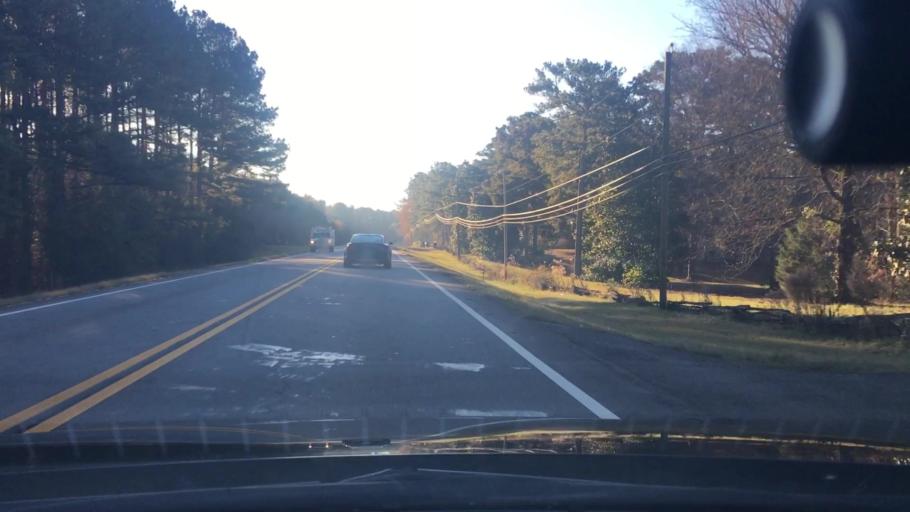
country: US
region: Georgia
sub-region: Coweta County
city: Senoia
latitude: 33.2906
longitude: -84.5418
